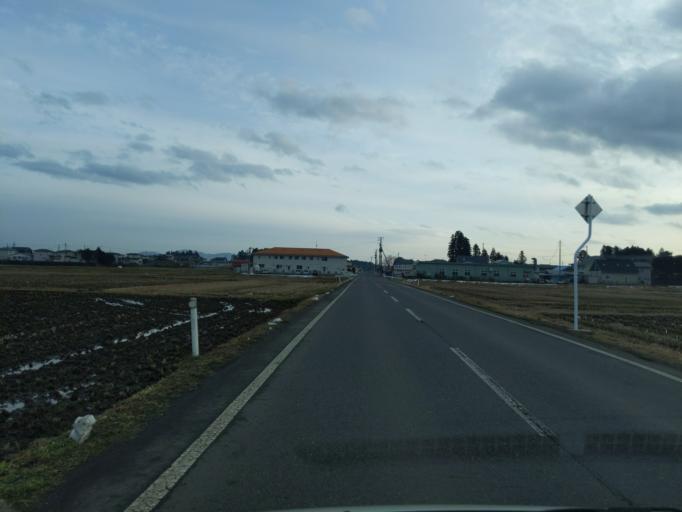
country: JP
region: Iwate
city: Mizusawa
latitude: 39.1371
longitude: 141.1145
